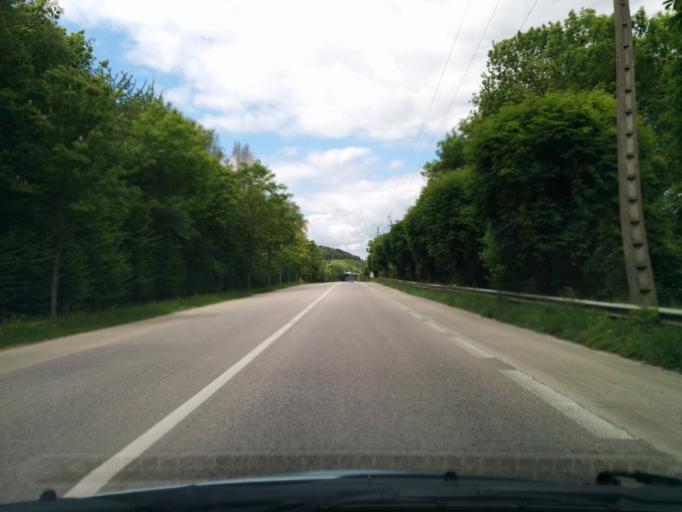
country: FR
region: Ile-de-France
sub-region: Departement des Yvelines
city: Porcheville
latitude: 48.9637
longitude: 1.7632
